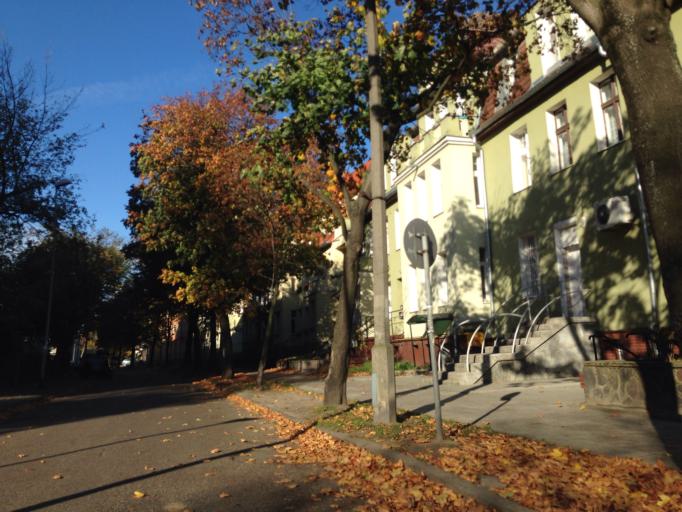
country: PL
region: Pomeranian Voivodeship
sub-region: Gdansk
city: Gdansk
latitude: 54.3758
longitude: 18.6265
